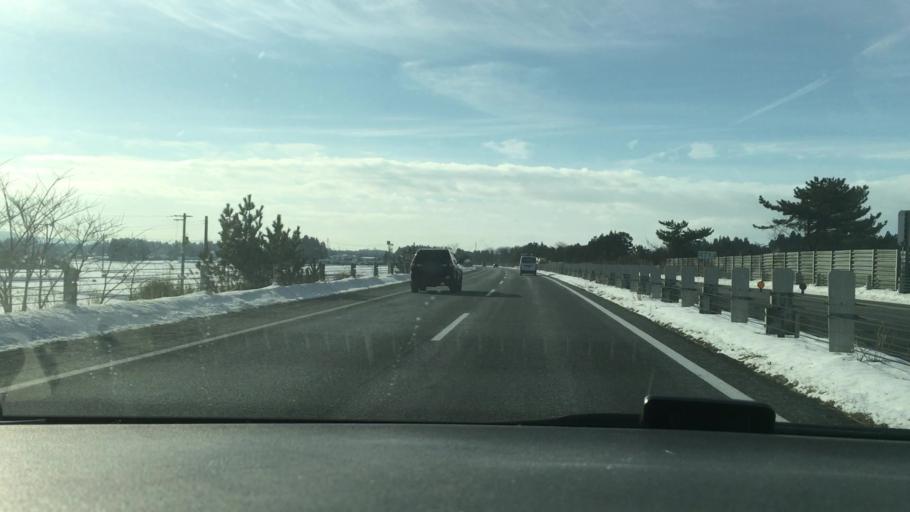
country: JP
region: Iwate
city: Hanamaki
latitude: 39.3596
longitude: 141.0898
